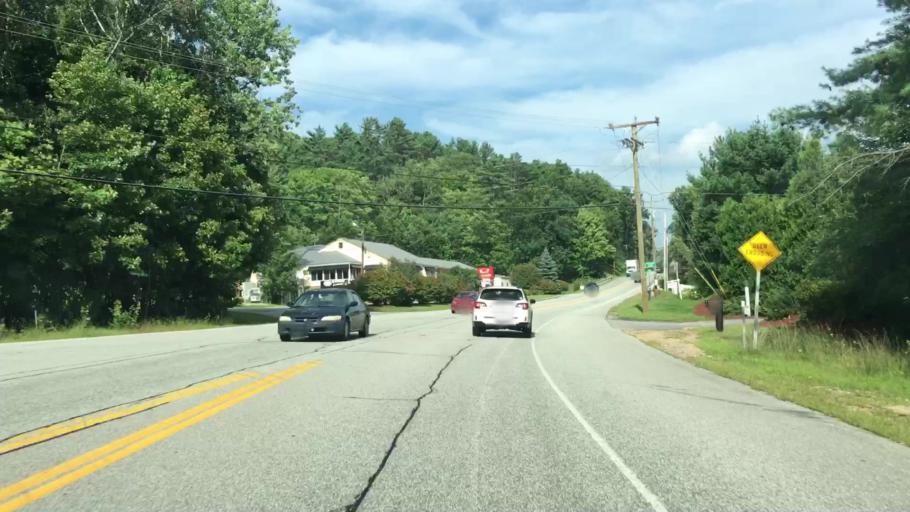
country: US
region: New Hampshire
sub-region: Belknap County
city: Sanbornton
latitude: 43.4845
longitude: -71.5368
